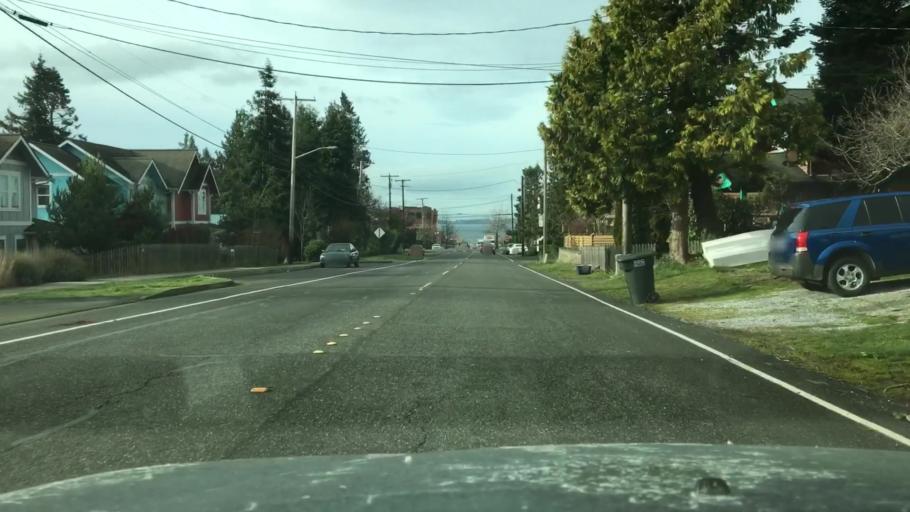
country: US
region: Washington
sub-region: Whatcom County
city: Bellingham
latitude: 48.7202
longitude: -122.4977
